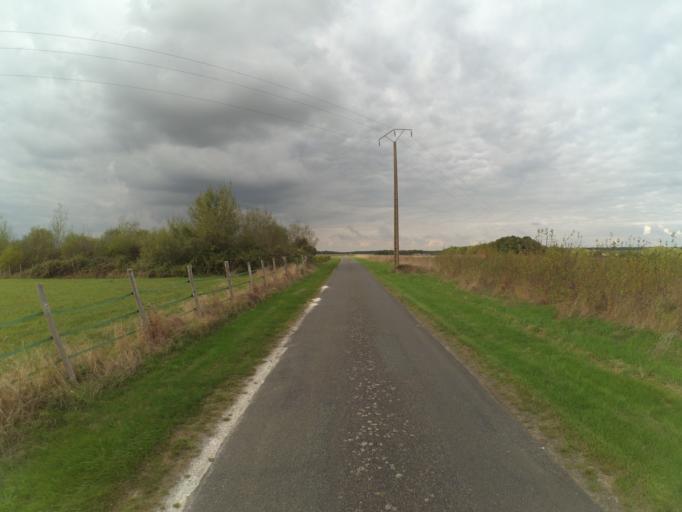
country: FR
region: Centre
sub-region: Departement d'Indre-et-Loire
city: Poce-sur-Cisse
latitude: 47.4881
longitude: 0.9769
